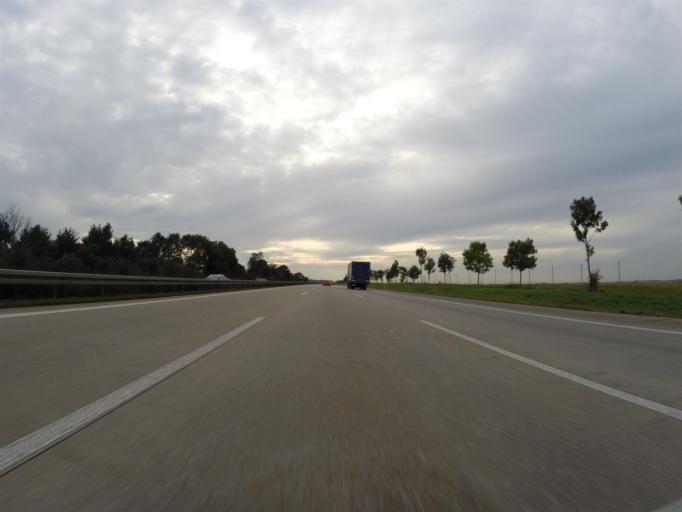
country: DE
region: Saxony
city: Wilsdruff
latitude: 51.0615
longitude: 13.5543
